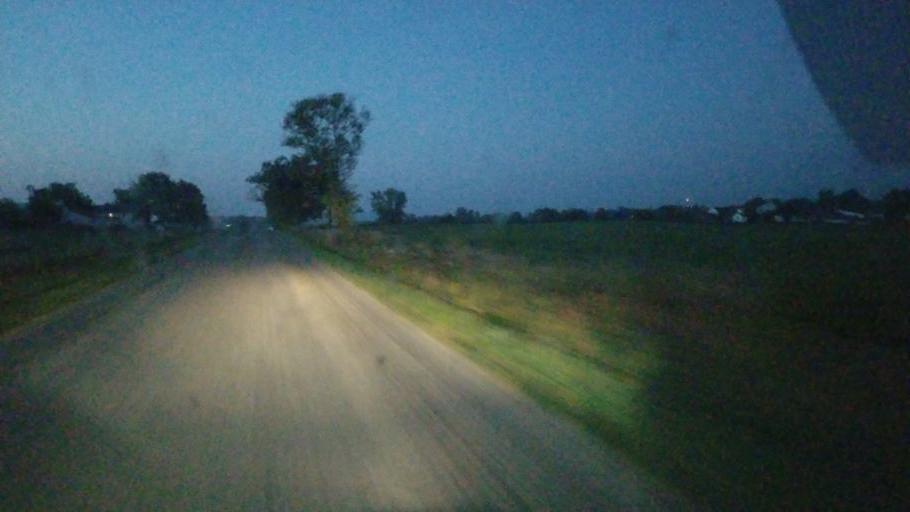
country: US
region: Indiana
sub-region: Elkhart County
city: Middlebury
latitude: 41.6884
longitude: -85.6678
